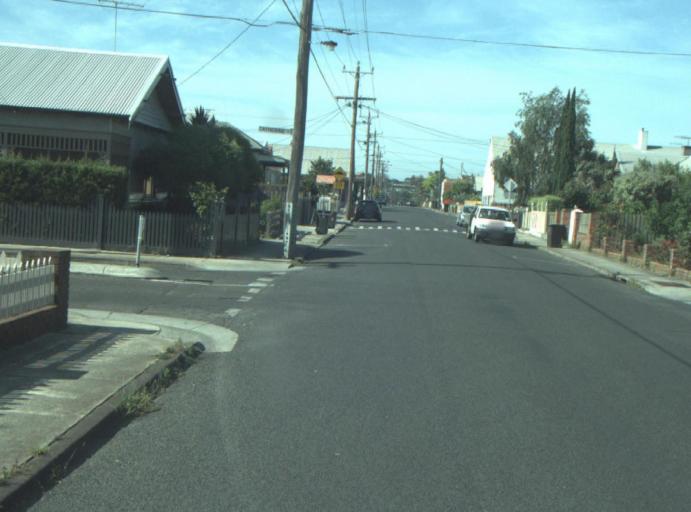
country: AU
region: Victoria
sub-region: Greater Geelong
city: Geelong West
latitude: -38.1380
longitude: 144.3404
